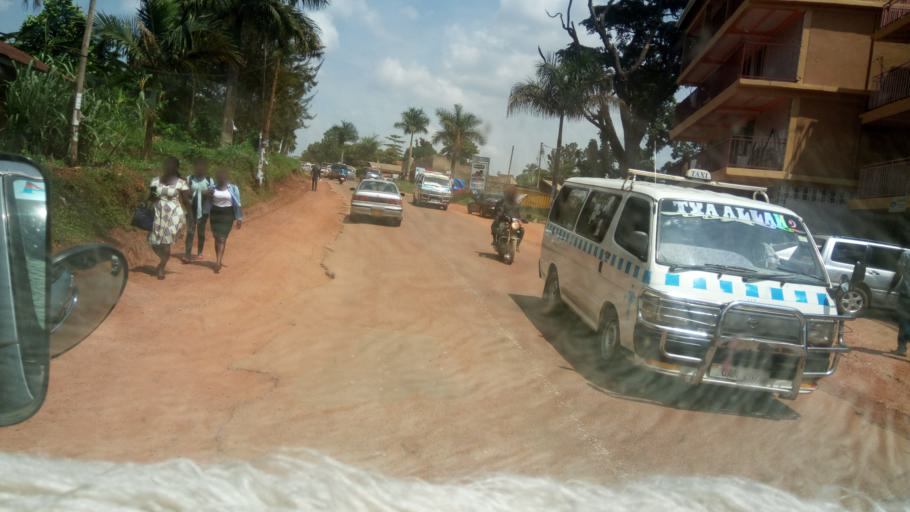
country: UG
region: Central Region
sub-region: Mukono District
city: Mukono
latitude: 0.3608
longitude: 32.7442
